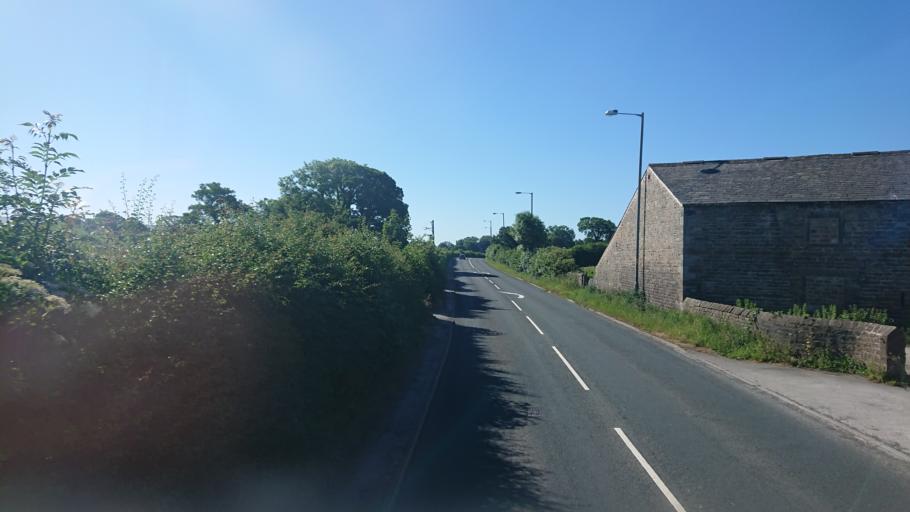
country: GB
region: England
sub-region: Lancashire
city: Galgate
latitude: 53.9862
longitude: -2.7888
